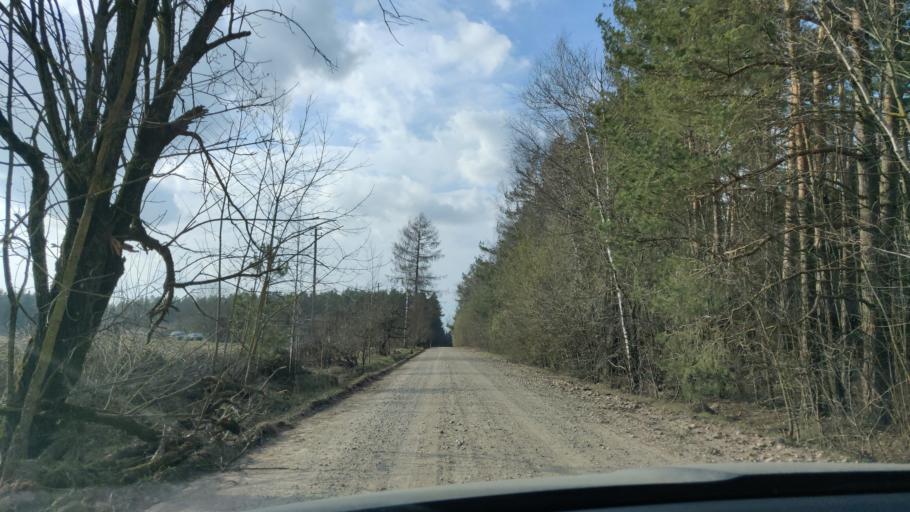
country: LT
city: Lentvaris
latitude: 54.5955
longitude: 25.0839
